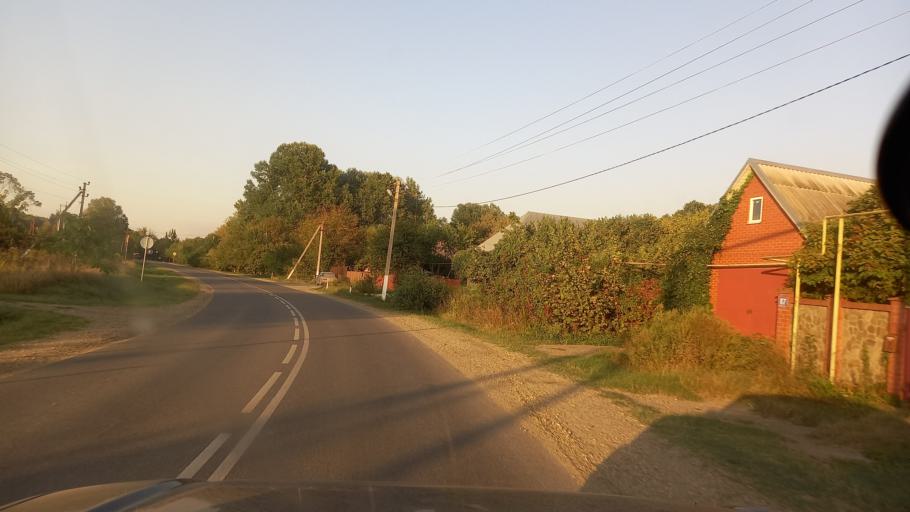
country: RU
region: Krasnodarskiy
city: Smolenskaya
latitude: 44.7653
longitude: 38.7775
